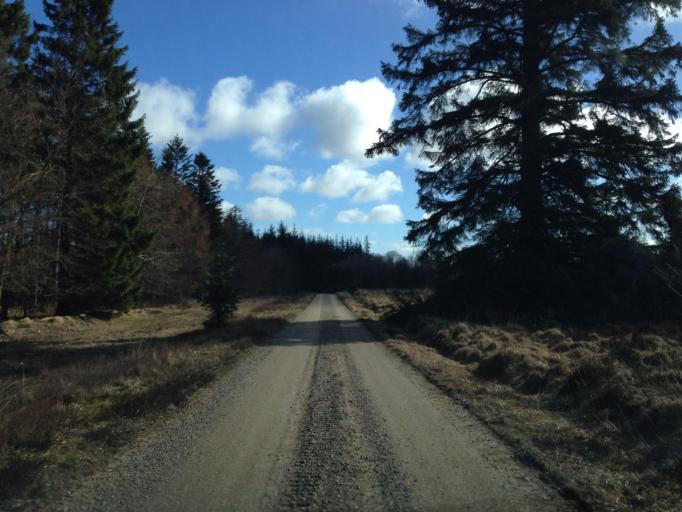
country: DK
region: Central Jutland
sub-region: Holstebro Kommune
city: Ulfborg
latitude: 56.2550
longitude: 8.4758
